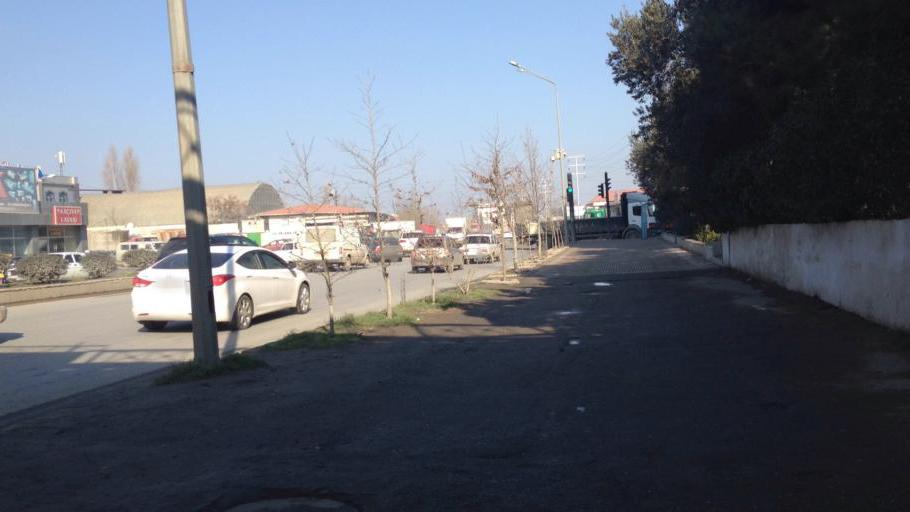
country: AZ
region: Baki
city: Binagadi
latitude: 40.4397
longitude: 49.8449
